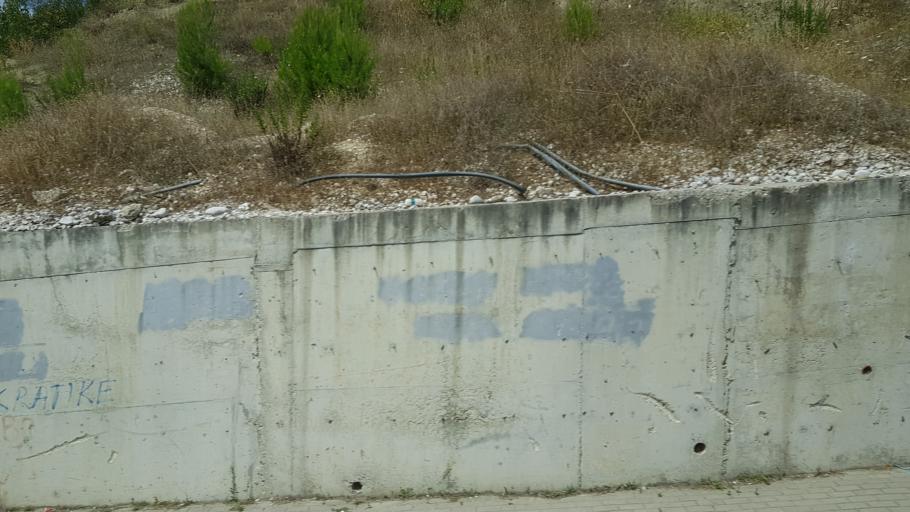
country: AL
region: Gjirokaster
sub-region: Rrethi i Tepelenes
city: Krahes
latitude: 40.4305
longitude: 19.8531
